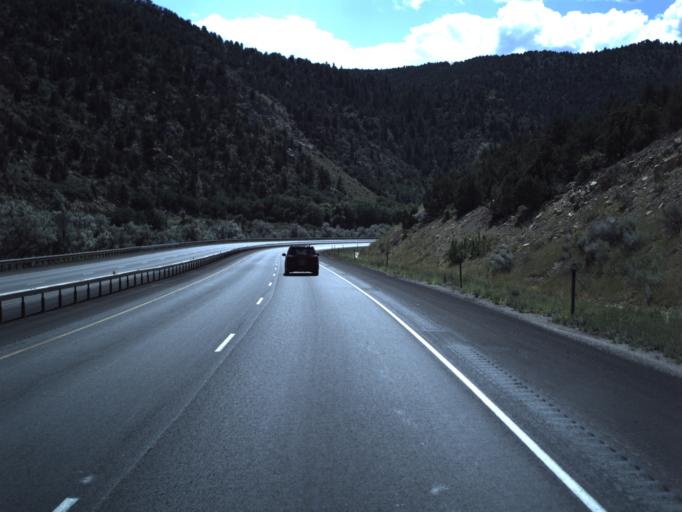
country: US
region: Utah
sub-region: Sevier County
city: Salina
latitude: 38.9025
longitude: -111.6435
